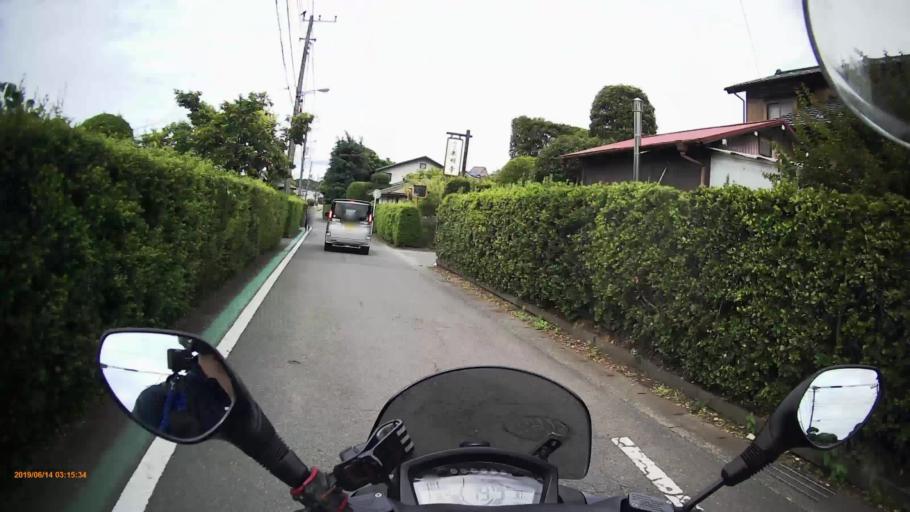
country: JP
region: Kanagawa
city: Minami-rinkan
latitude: 35.4139
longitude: 139.4591
